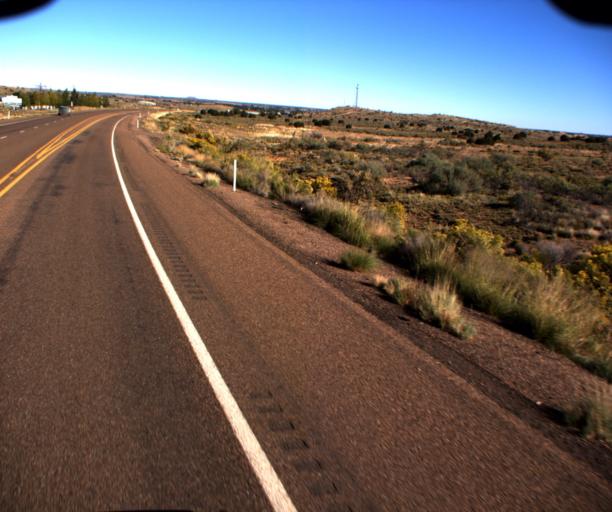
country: US
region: Arizona
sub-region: Navajo County
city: Taylor
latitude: 34.4347
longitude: -110.0946
